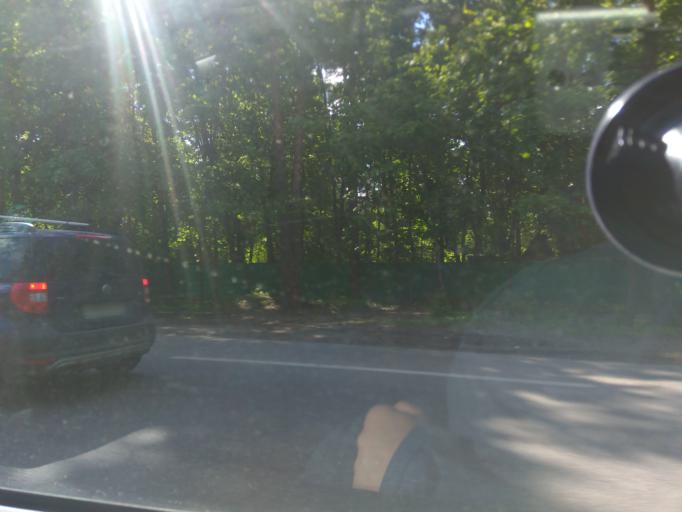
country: RU
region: Moskovskaya
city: Kratovo
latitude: 55.5718
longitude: 38.1832
